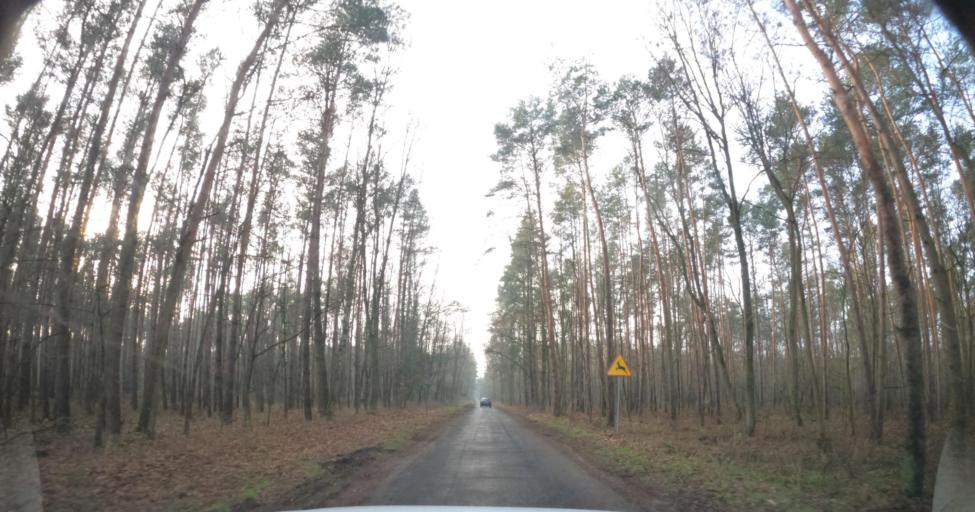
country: PL
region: West Pomeranian Voivodeship
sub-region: Powiat mysliborski
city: Boleszkowice
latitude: 52.7168
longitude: 14.5606
